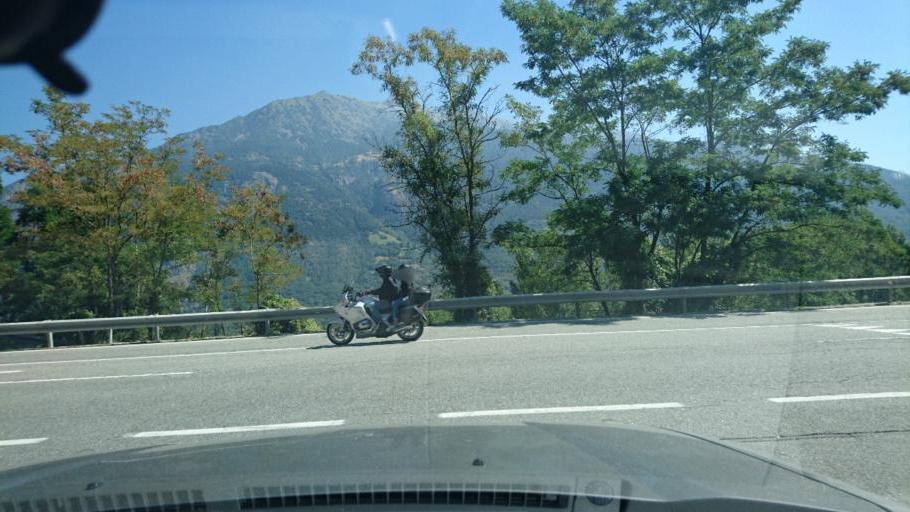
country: IT
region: Aosta Valley
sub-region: Valle d'Aosta
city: Gignod
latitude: 45.7850
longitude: 7.2957
